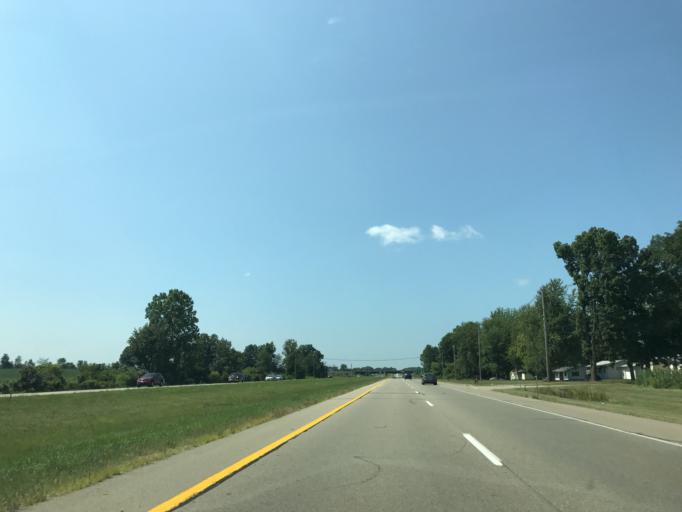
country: US
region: Michigan
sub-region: Berrien County
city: Niles
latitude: 41.8052
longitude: -86.3071
